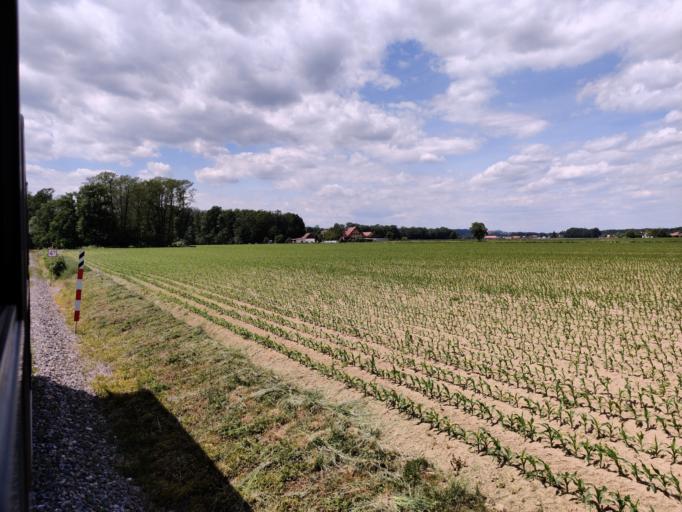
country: AT
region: Styria
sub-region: Politischer Bezirk Suedoststeiermark
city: Halbenrain
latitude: 46.7331
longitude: 15.9151
